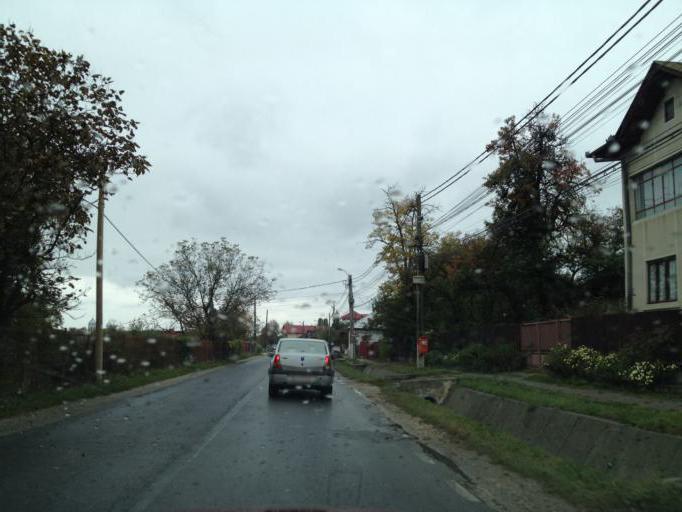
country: RO
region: Arges
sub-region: Comuna Valea Mare-Pravat
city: Valea Mare Pravat
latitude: 45.2935
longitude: 25.0938
